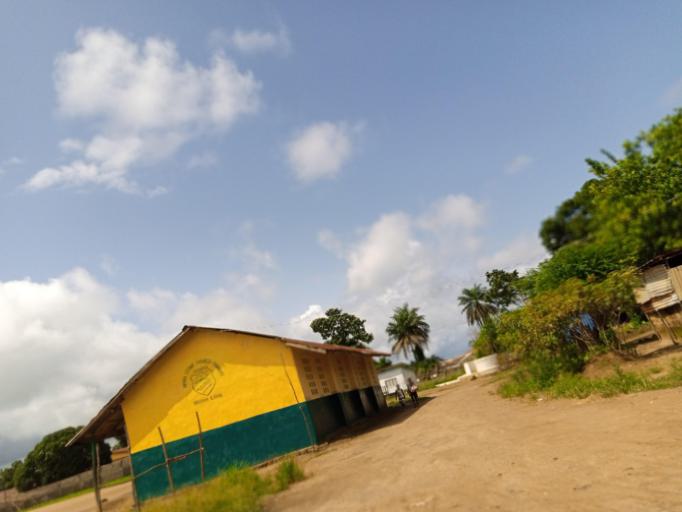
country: SL
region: Northern Province
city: Tintafor
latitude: 8.6253
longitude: -13.2131
